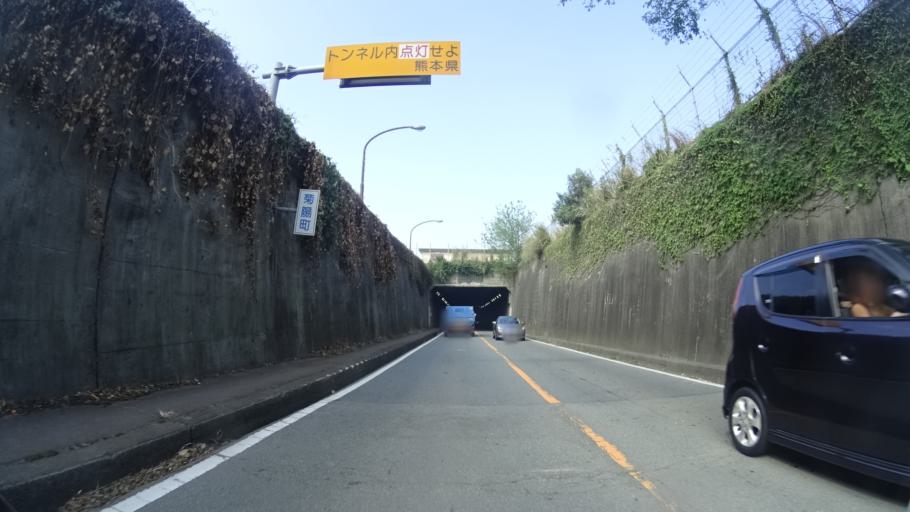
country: JP
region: Kumamoto
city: Ozu
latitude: 32.8343
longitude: 130.8555
